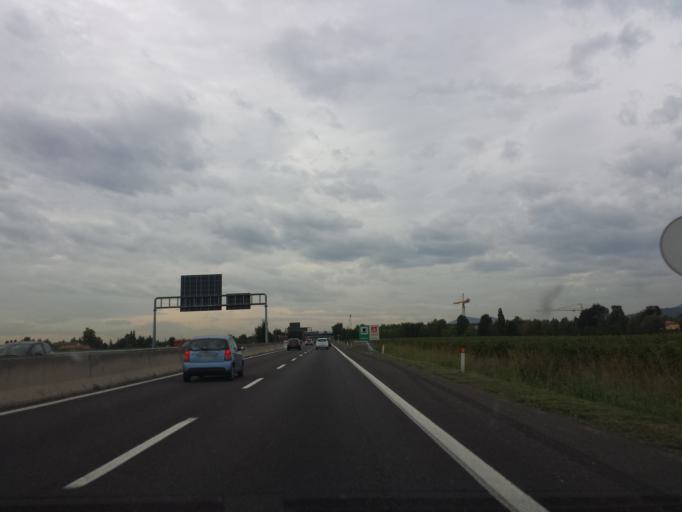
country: IT
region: Veneto
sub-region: Provincia di Padova
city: Terradura
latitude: 45.3300
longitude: 11.8366
